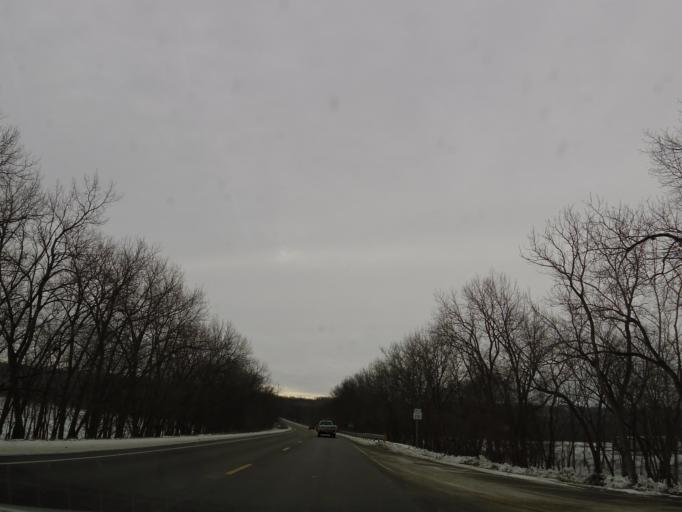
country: US
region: Illinois
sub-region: LaSalle County
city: Peru
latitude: 41.3142
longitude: -89.1187
